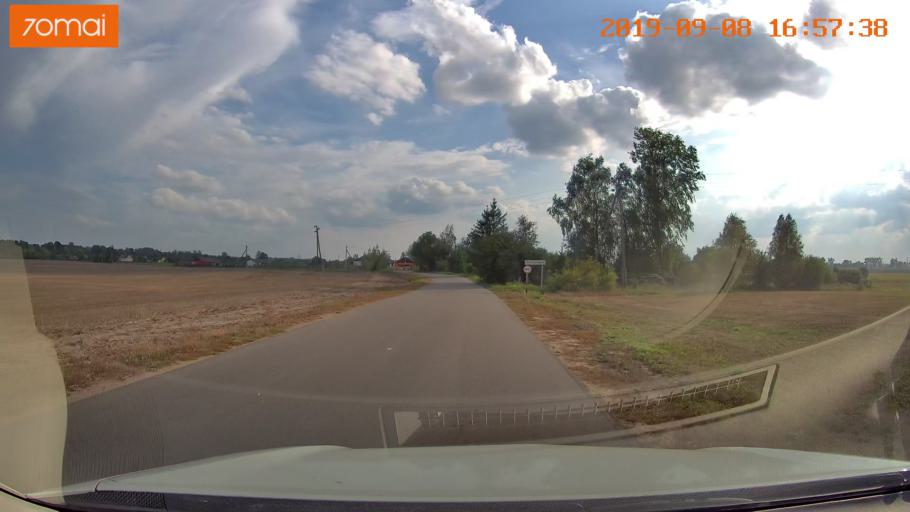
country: BY
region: Grodnenskaya
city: Hrodna
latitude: 53.7308
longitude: 23.9274
